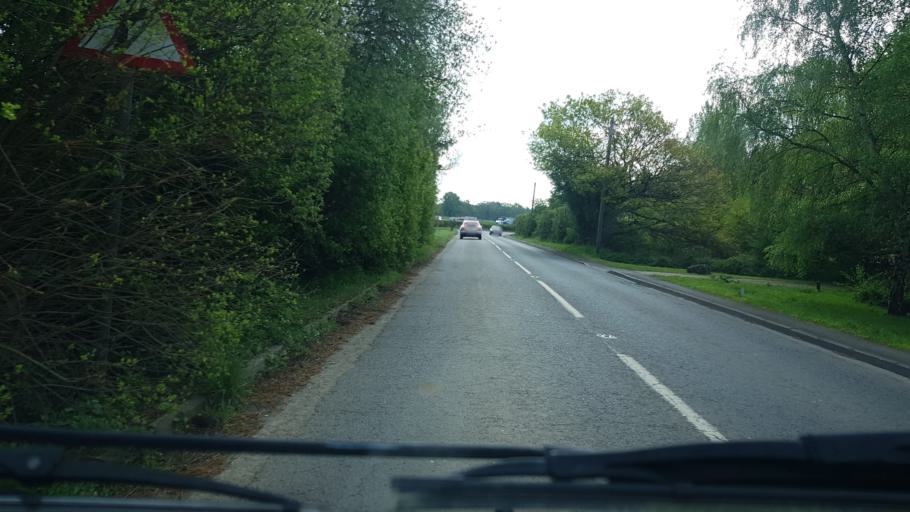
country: GB
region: England
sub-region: Surrey
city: Leatherhead
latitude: 51.3105
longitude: -0.3515
